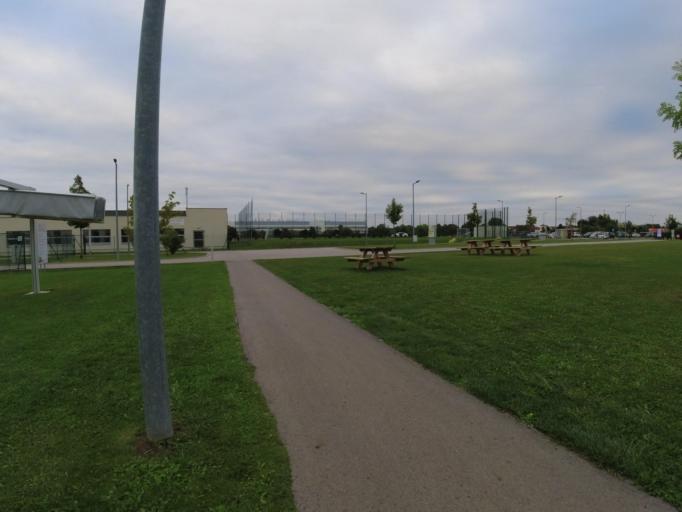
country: AT
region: Lower Austria
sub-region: Politischer Bezirk Wien-Umgebung
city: Gerasdorf bei Wien
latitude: 48.2546
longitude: 16.4778
